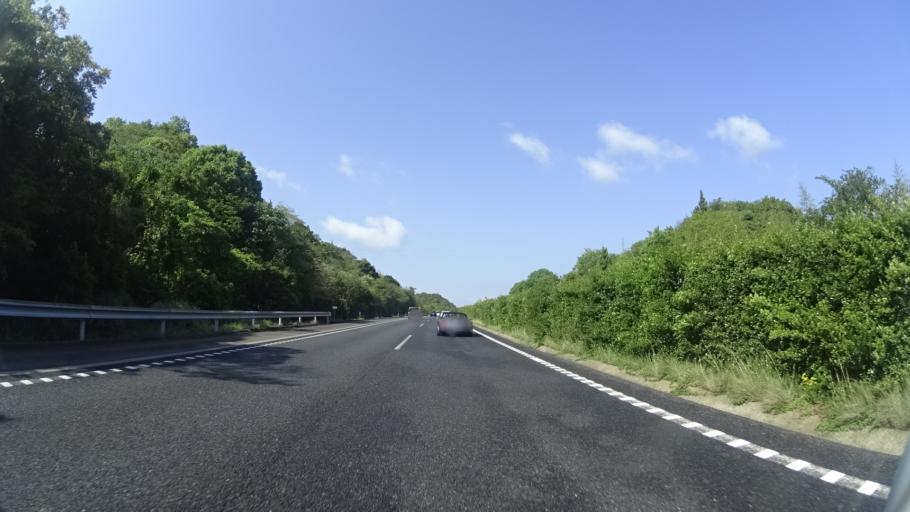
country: JP
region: Hyogo
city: Fukura
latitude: 34.2774
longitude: 134.7048
